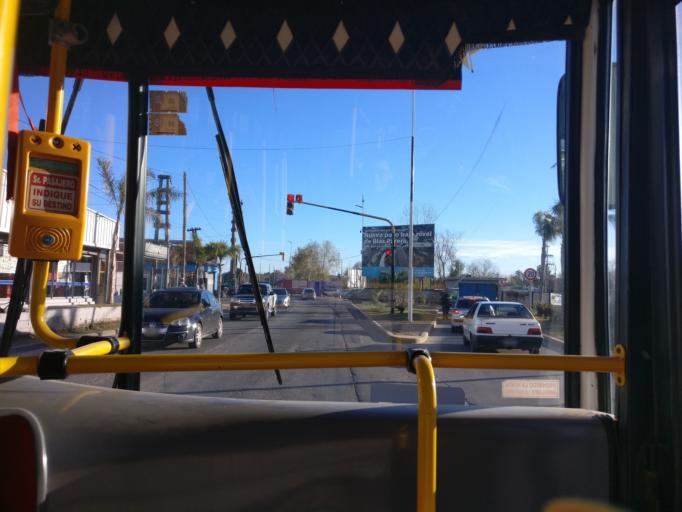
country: AR
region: Buenos Aires
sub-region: Partido de Ezeiza
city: Ezeiza
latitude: -34.8930
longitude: -58.5720
